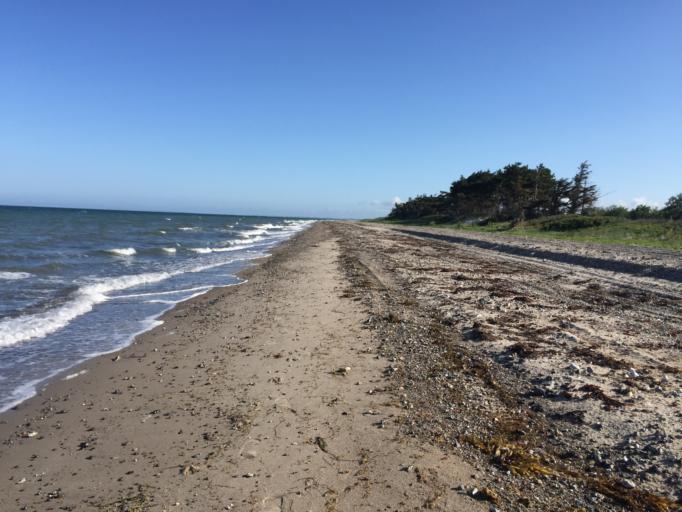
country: DK
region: Zealand
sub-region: Slagelse Kommune
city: Korsor
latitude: 55.2111
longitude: 11.1726
